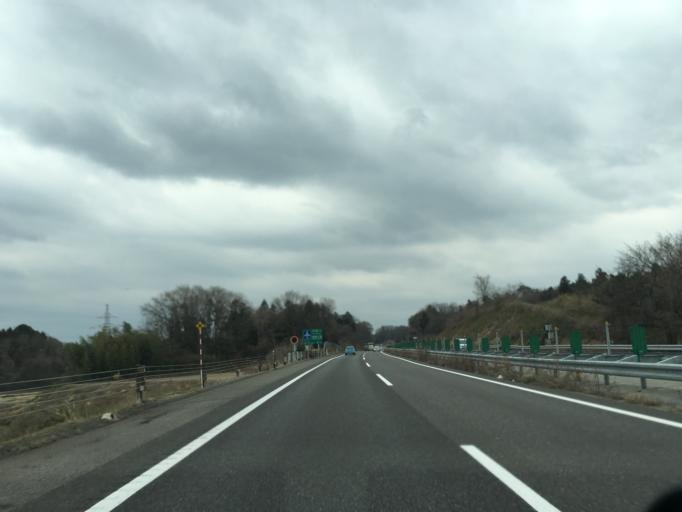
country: JP
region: Fukushima
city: Sukagawa
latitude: 37.3186
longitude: 140.3430
